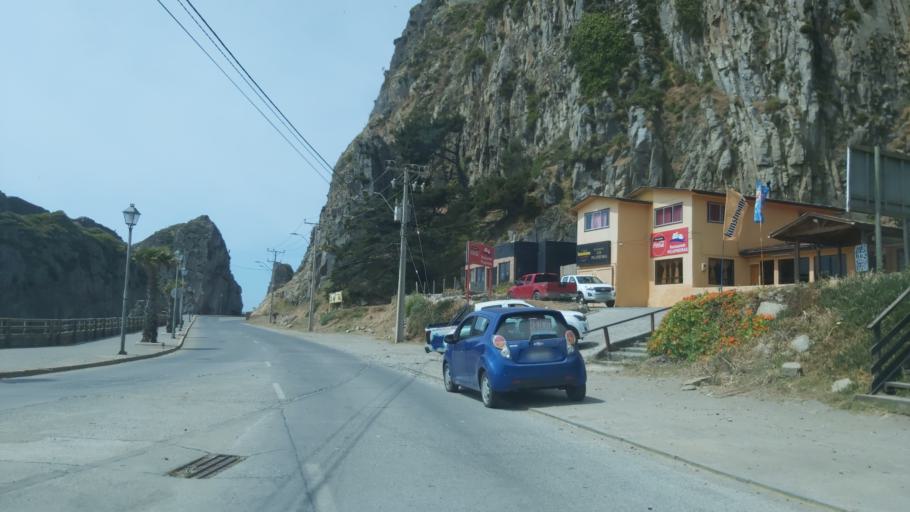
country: CL
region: Maule
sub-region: Provincia de Talca
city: Constitucion
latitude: -35.3279
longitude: -72.4298
